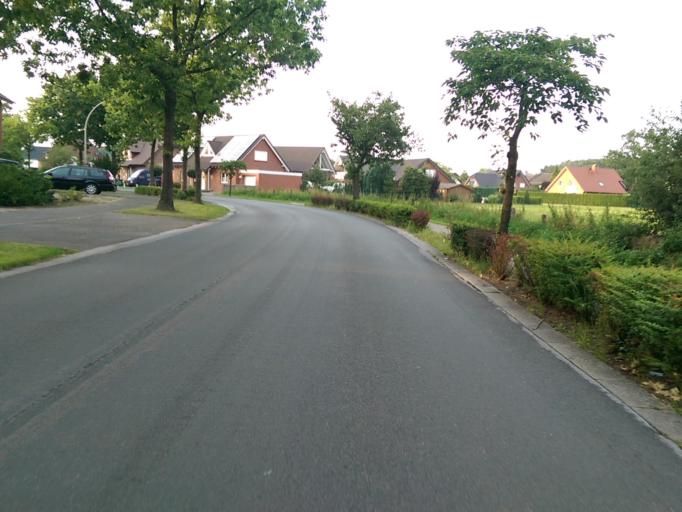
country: DE
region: North Rhine-Westphalia
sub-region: Regierungsbezirk Detmold
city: Rheda-Wiedenbruck
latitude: 51.8864
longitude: 8.2346
